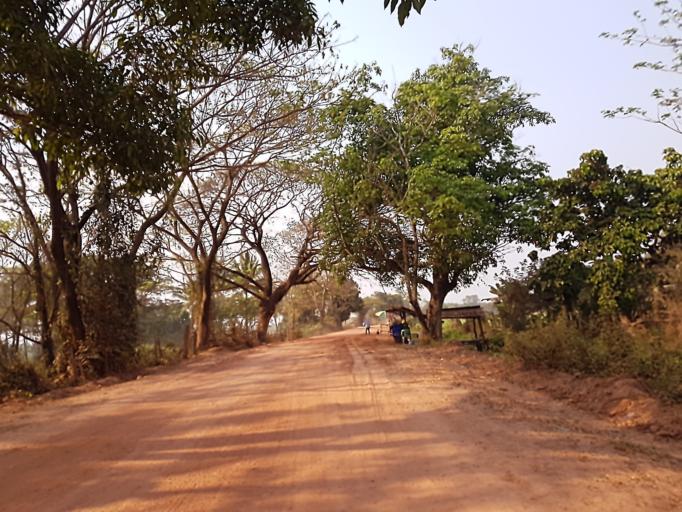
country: TH
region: Nong Khai
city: Phon Phisai
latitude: 18.0014
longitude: 102.9081
